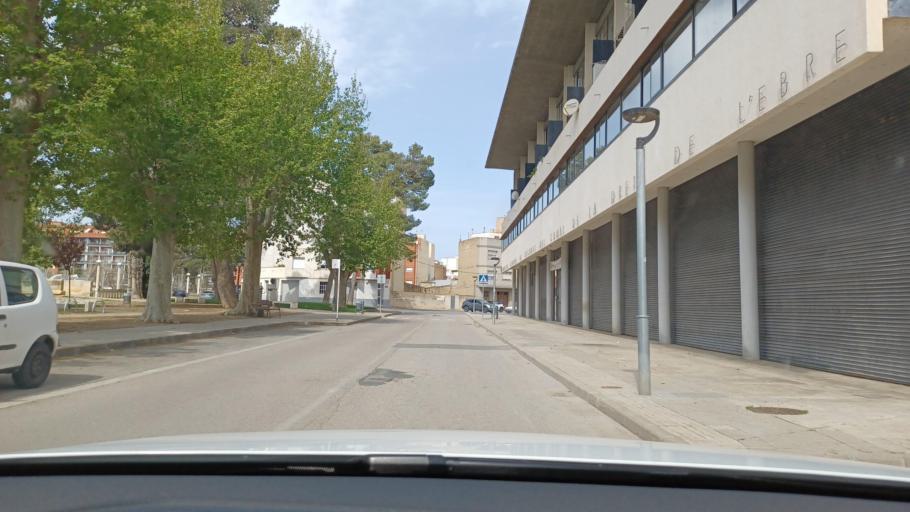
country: ES
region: Catalonia
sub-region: Provincia de Tarragona
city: Amposta
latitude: 40.7105
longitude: 0.5843
